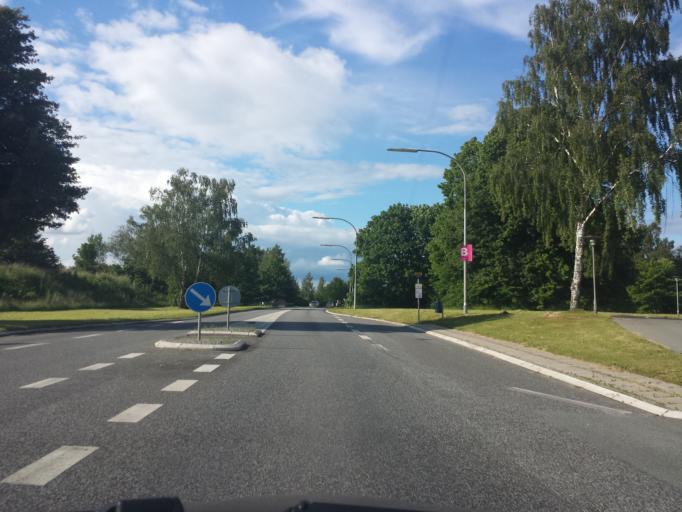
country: DK
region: Capital Region
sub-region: Ballerup Kommune
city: Malov
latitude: 55.7482
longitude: 12.3297
